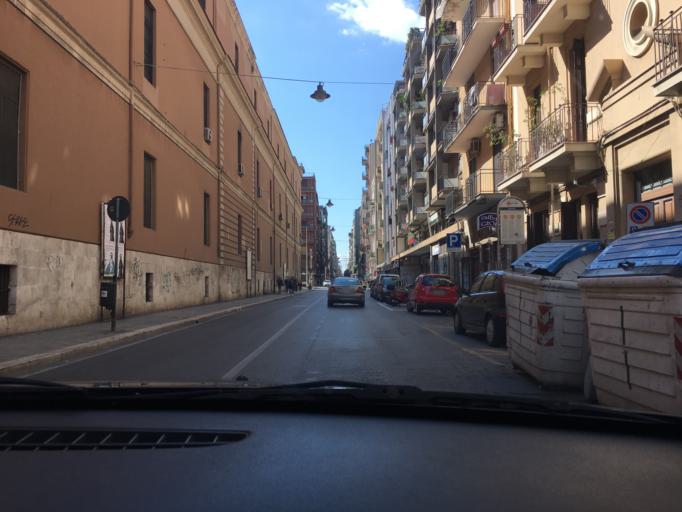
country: IT
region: Apulia
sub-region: Provincia di Bari
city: Bari
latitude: 41.1202
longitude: 16.8756
